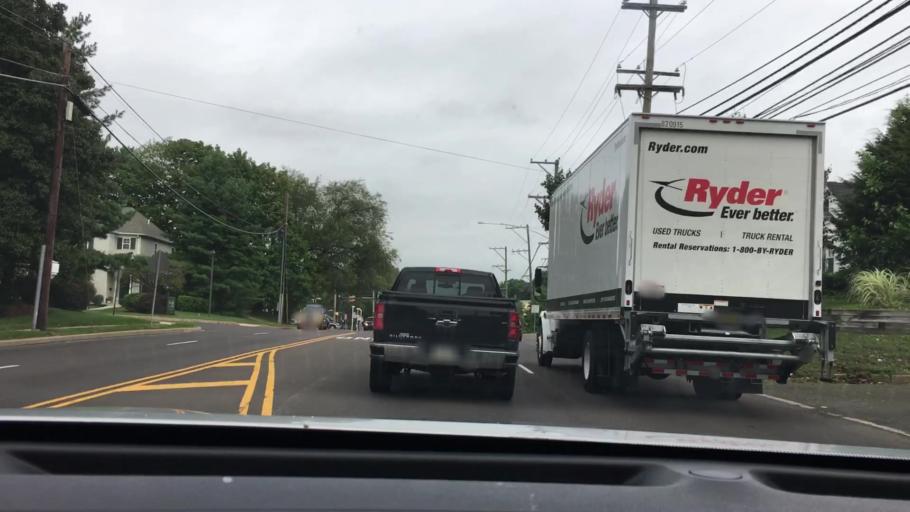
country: US
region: Pennsylvania
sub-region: Montgomery County
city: Hatboro
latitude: 40.1892
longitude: -75.1015
